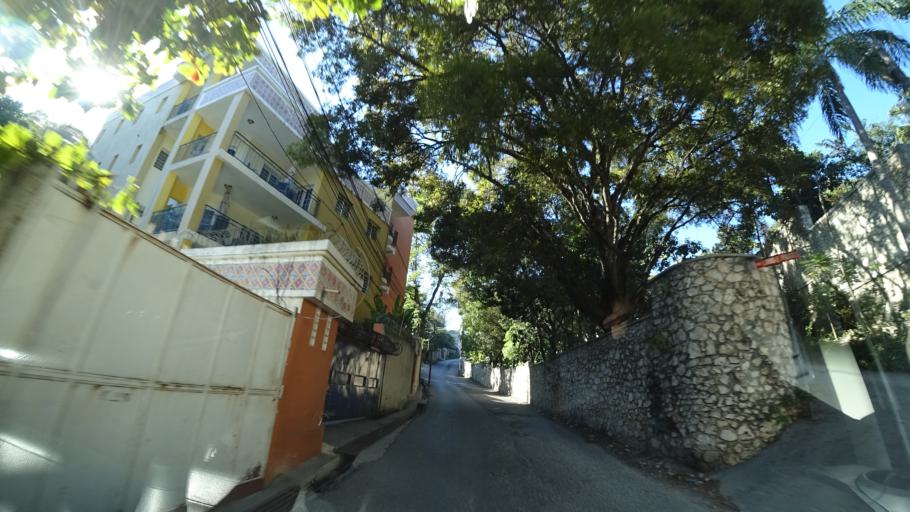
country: HT
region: Ouest
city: Petionville
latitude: 18.5064
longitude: -72.2900
